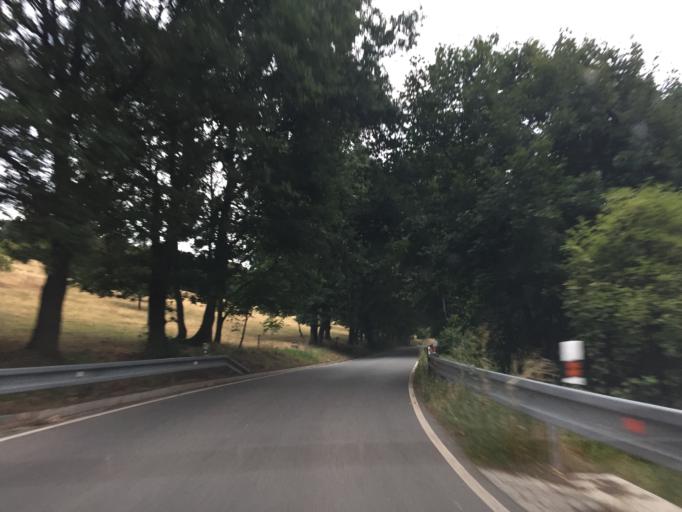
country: CZ
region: Liberecky
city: Mala Skala
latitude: 50.6501
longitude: 15.1978
